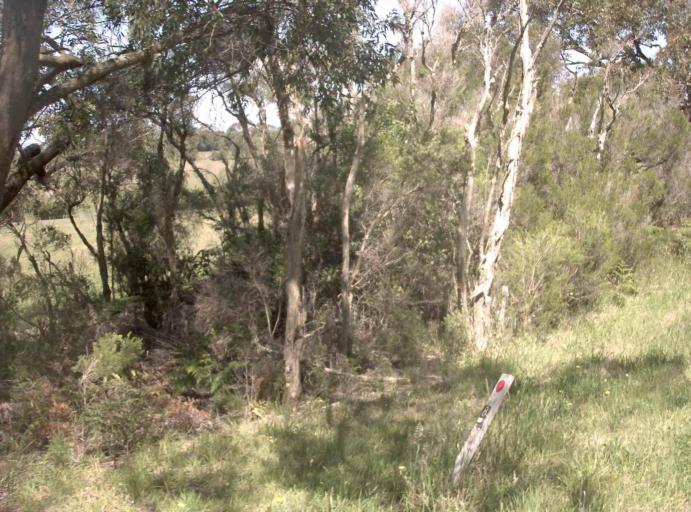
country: AU
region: Victoria
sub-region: Bass Coast
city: North Wonthaggi
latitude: -38.7698
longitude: 146.0648
